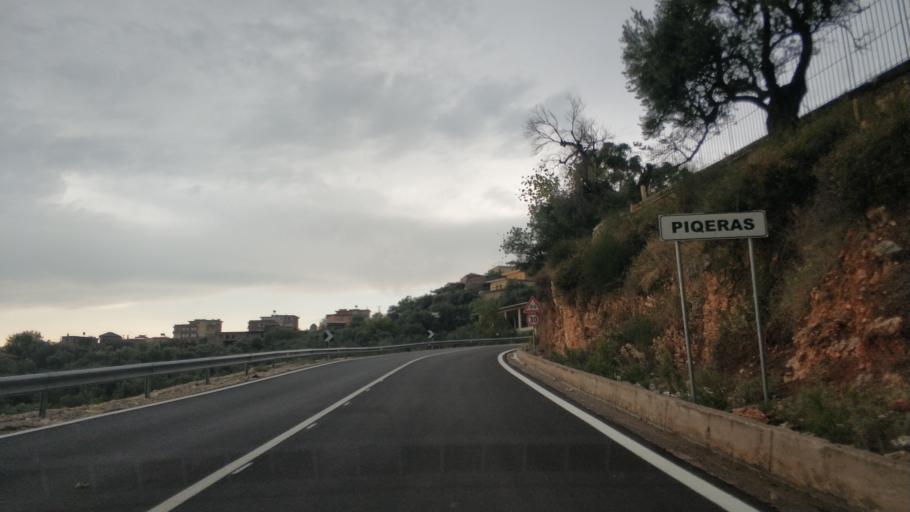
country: AL
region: Vlore
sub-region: Rrethi i Sarandes
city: Lukove
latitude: 40.0144
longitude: 19.8948
